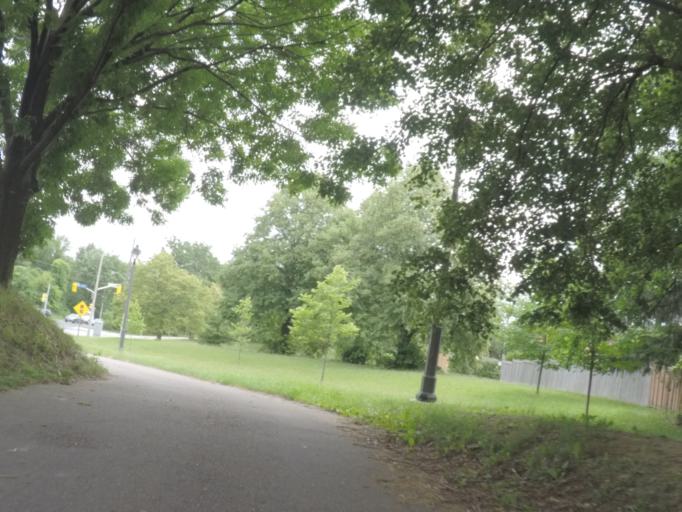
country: CA
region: Ontario
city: Etobicoke
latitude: 43.6804
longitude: -79.5337
